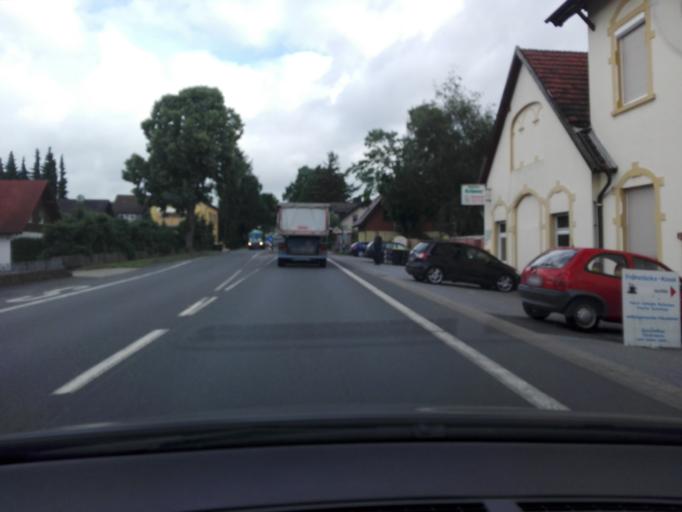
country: DE
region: North Rhine-Westphalia
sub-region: Regierungsbezirk Arnsberg
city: Unna
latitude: 51.4874
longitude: 7.7069
